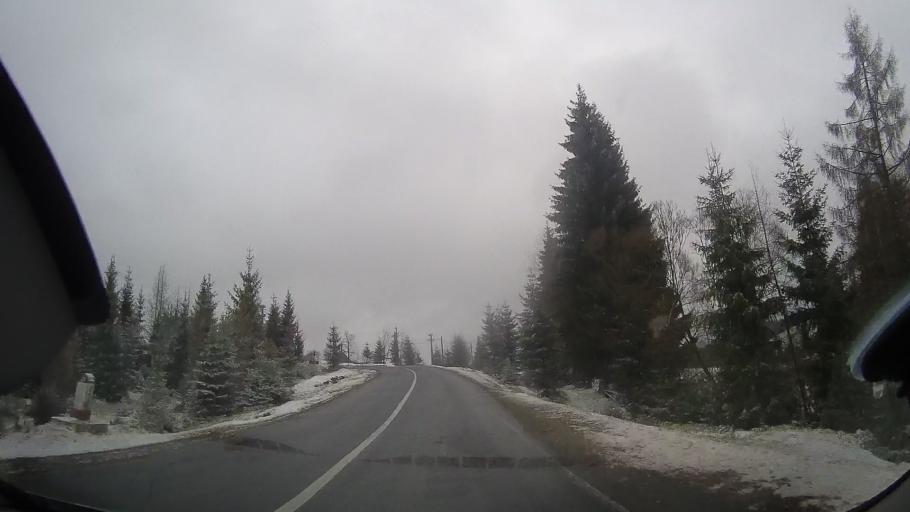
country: RO
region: Cluj
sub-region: Comuna Belis
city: Belis
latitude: 46.6912
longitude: 23.0389
